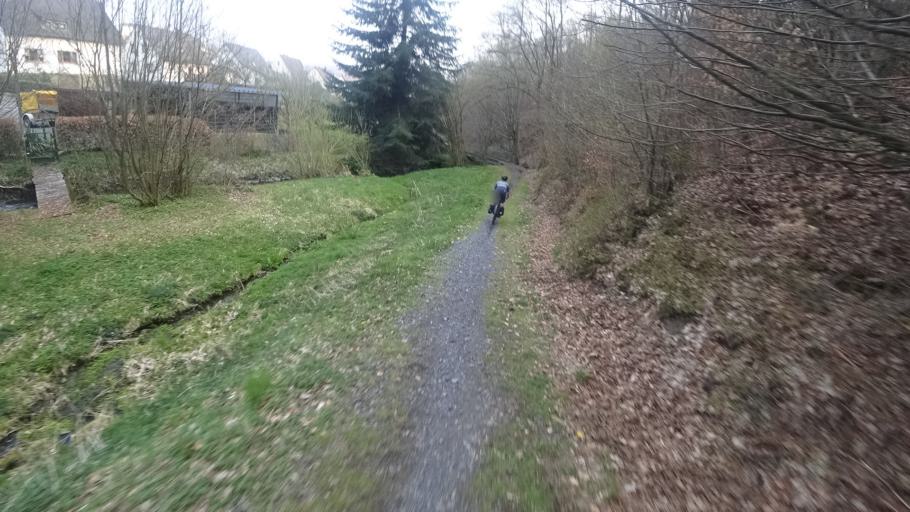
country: DE
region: Rheinland-Pfalz
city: Luckenbach
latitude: 50.7026
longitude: 7.8311
